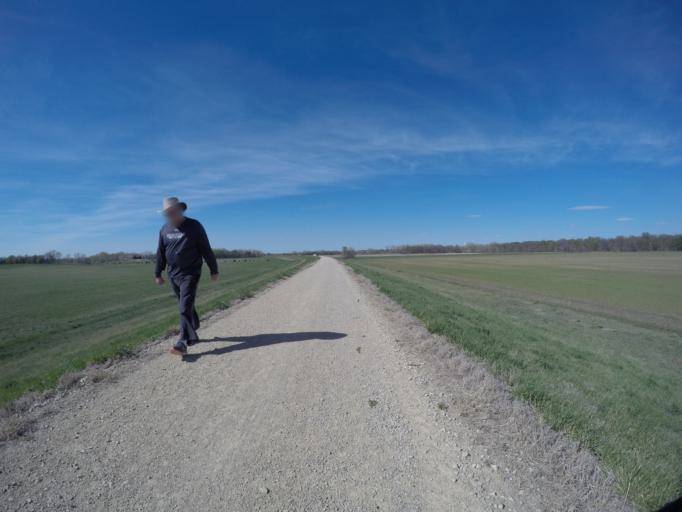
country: US
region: Kansas
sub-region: Saline County
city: Salina
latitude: 38.7886
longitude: -97.5761
